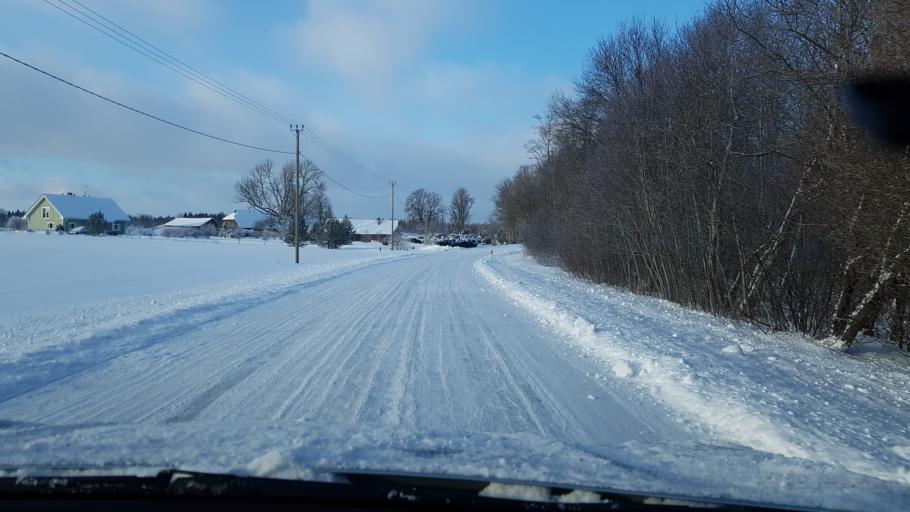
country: EE
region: Harju
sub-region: Nissi vald
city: Turba
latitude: 59.1071
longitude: 24.2318
